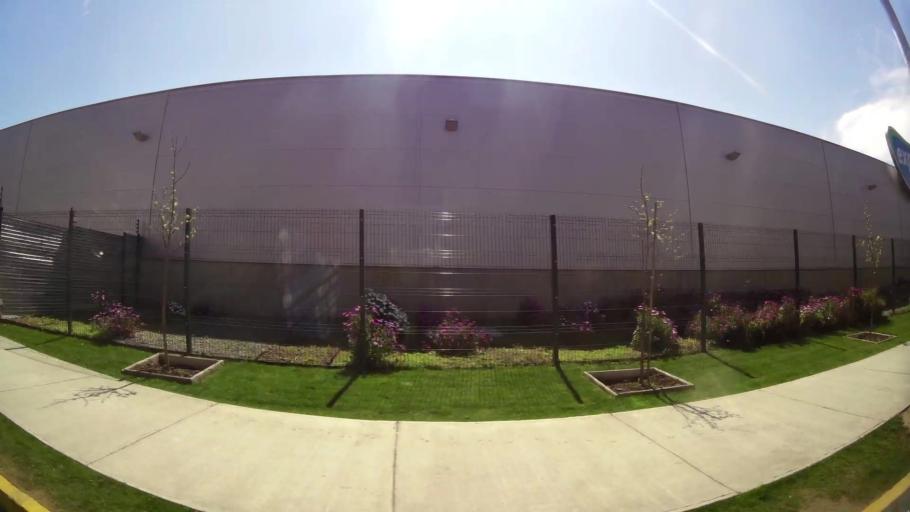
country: CL
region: Santiago Metropolitan
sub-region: Provincia de Santiago
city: Lo Prado
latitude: -33.4851
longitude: -70.7395
